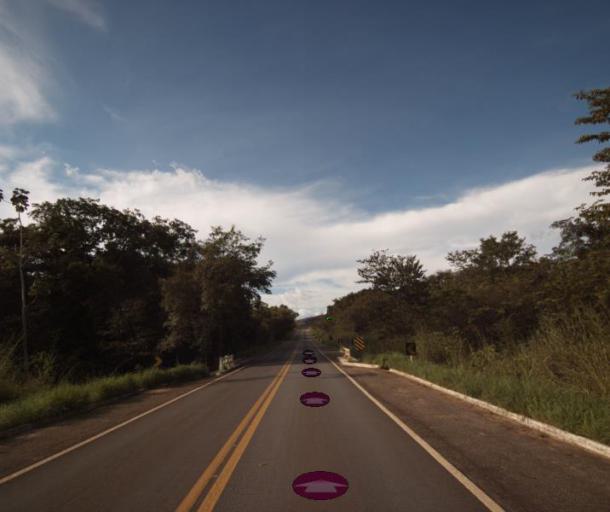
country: BR
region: Goias
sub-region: Barro Alto
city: Barro Alto
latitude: -14.9914
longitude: -48.6813
